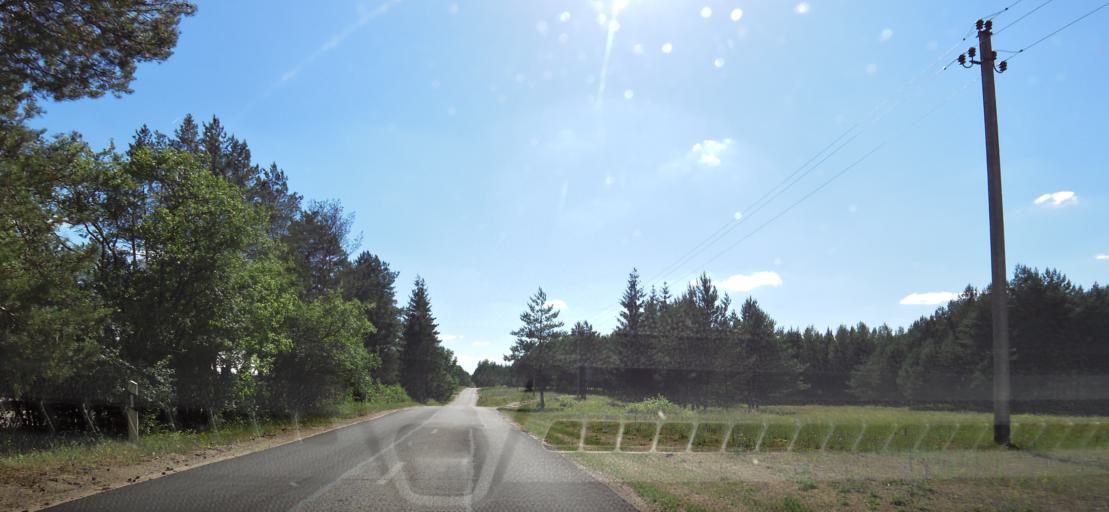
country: LT
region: Vilnius County
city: Rasos
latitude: 54.7595
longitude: 25.3455
